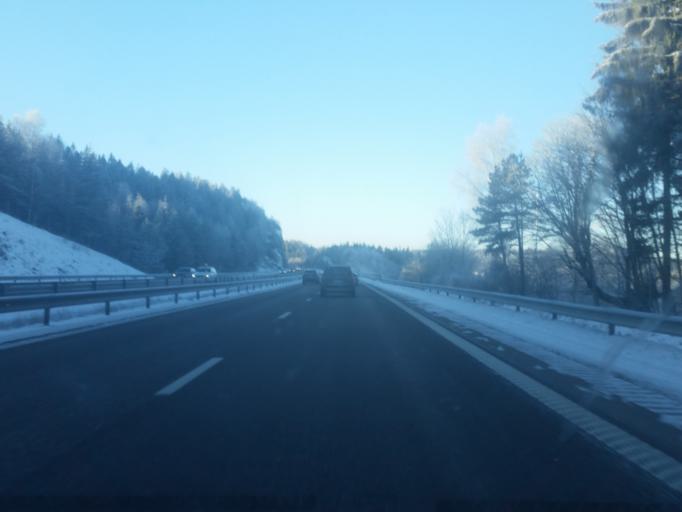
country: SE
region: Vaestra Goetaland
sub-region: Harryda Kommun
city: Landvetter
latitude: 57.6858
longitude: 12.2843
